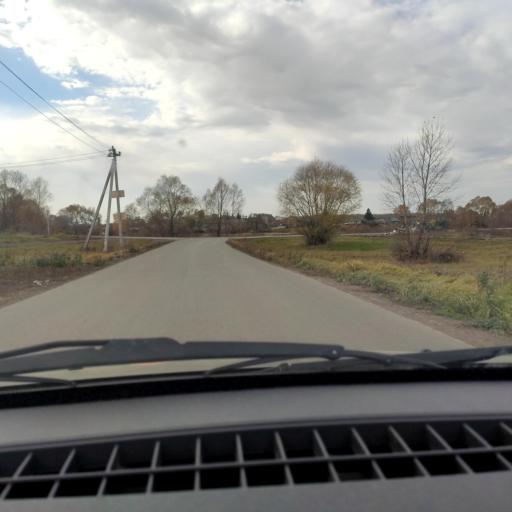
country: RU
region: Bashkortostan
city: Ufa
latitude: 54.6098
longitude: 55.9065
